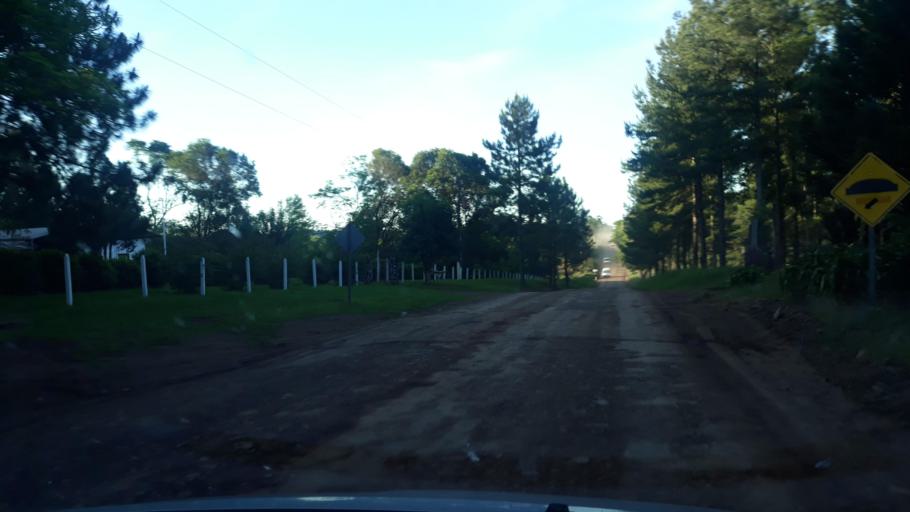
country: AR
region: Misiones
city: Ruiz de Montoya
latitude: -27.0573
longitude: -55.0050
